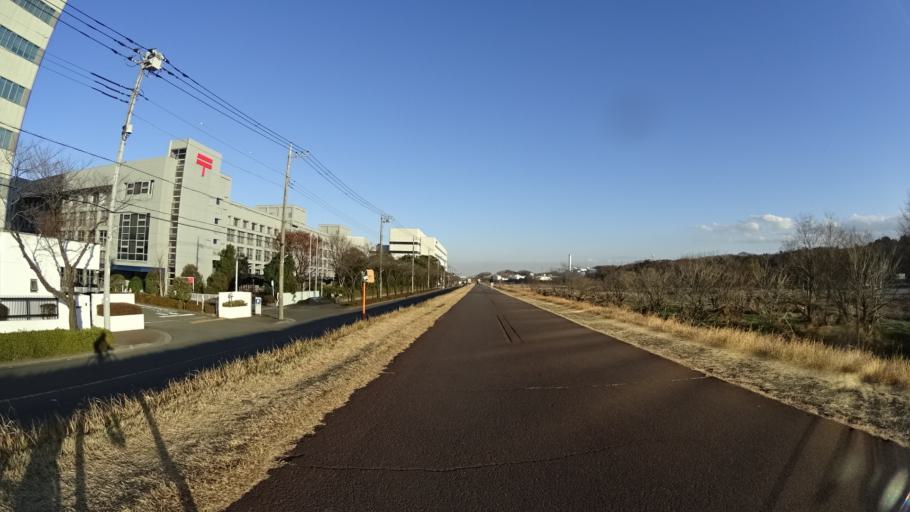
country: JP
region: Tokyo
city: Kokubunji
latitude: 35.6542
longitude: 139.4616
